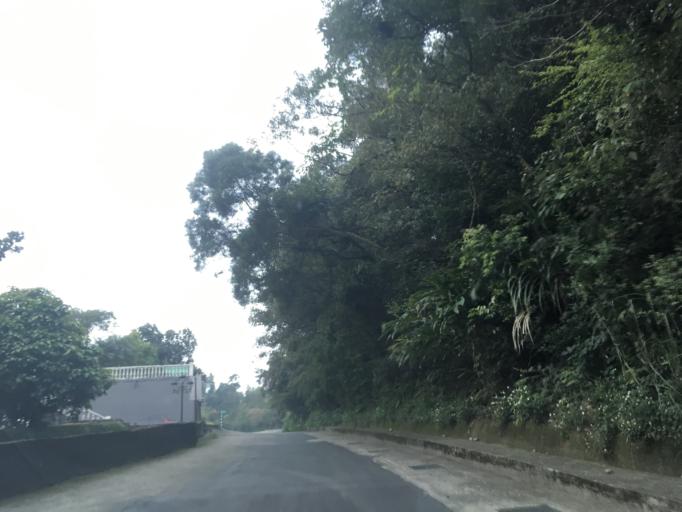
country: TW
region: Taiwan
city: Daxi
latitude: 24.8855
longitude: 121.3008
